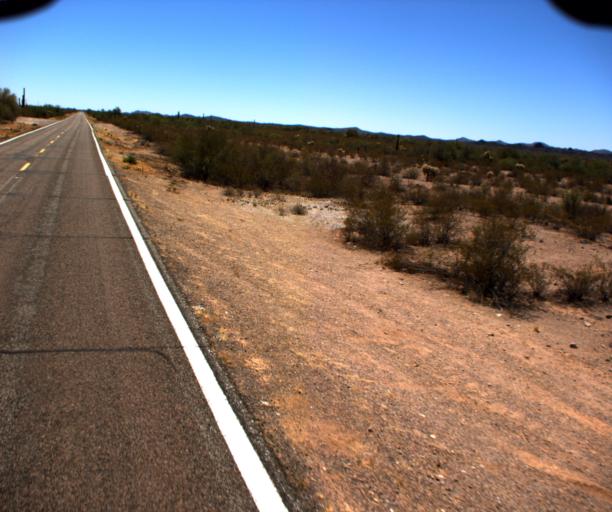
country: US
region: Arizona
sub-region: Pima County
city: Ajo
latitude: 32.2218
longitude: -112.6681
